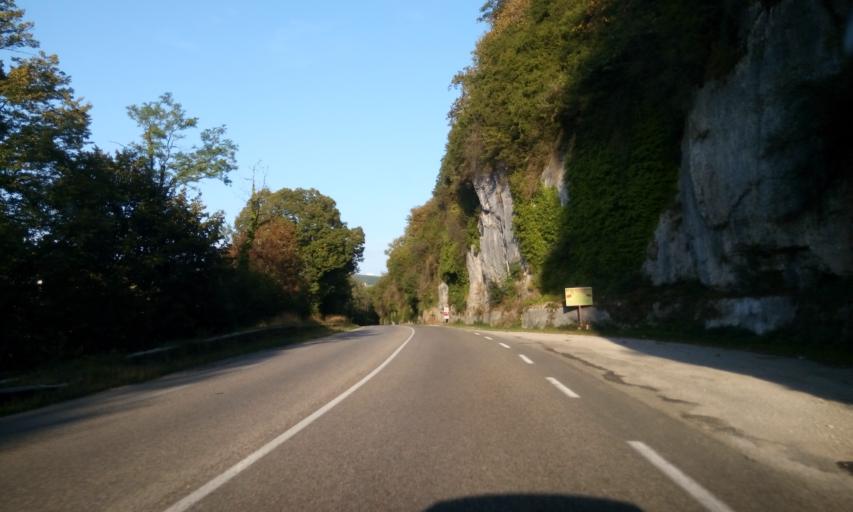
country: FR
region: Rhone-Alpes
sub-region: Departement de l'Ain
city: Neuville-sur-Ain
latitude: 46.0835
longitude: 5.3906
